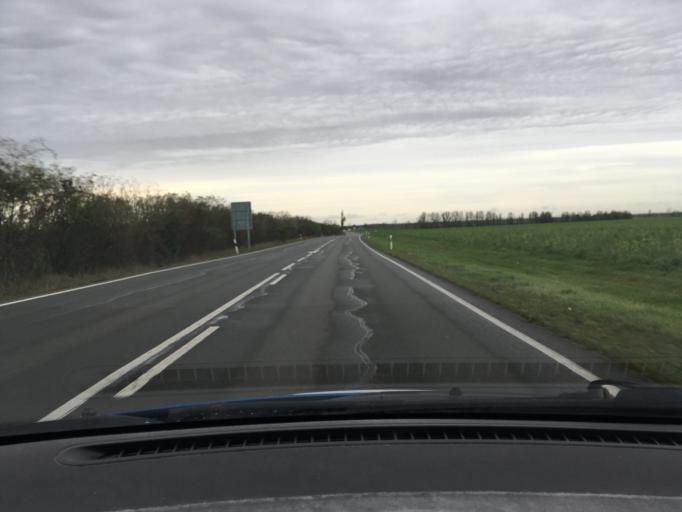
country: DE
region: Saxony-Anhalt
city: Zerbst
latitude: 51.9931
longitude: 12.0409
